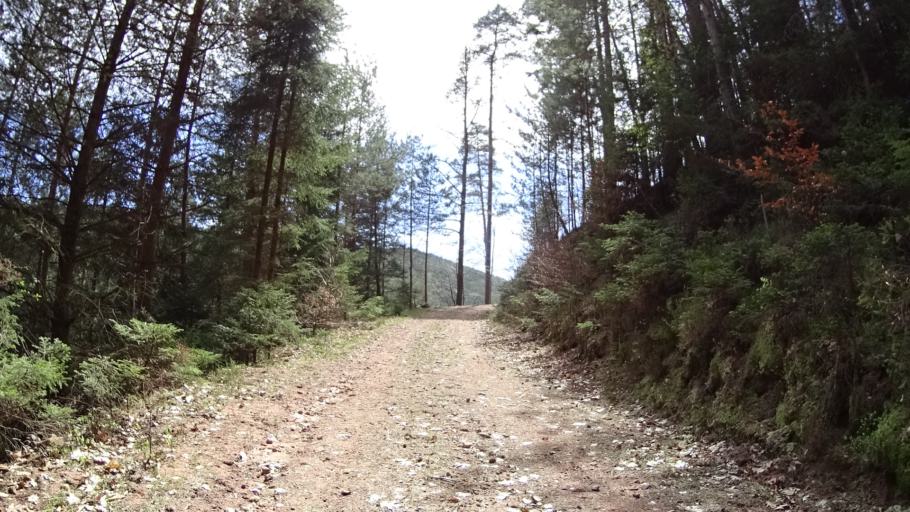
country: DE
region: Rheinland-Pfalz
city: Ramberg
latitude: 49.3130
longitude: 7.9941
